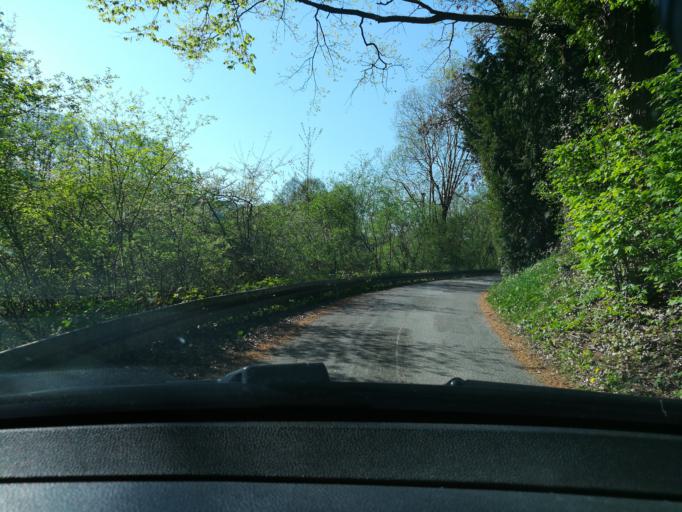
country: DE
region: North Rhine-Westphalia
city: Borgholzhausen
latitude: 52.1095
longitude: 8.3046
